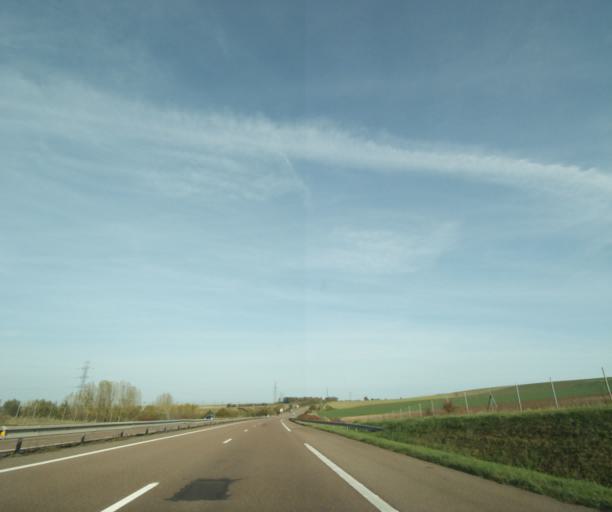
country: FR
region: Champagne-Ardenne
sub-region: Departement de la Marne
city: Jonchery-sur-Vesle
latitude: 49.2030
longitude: 3.7661
